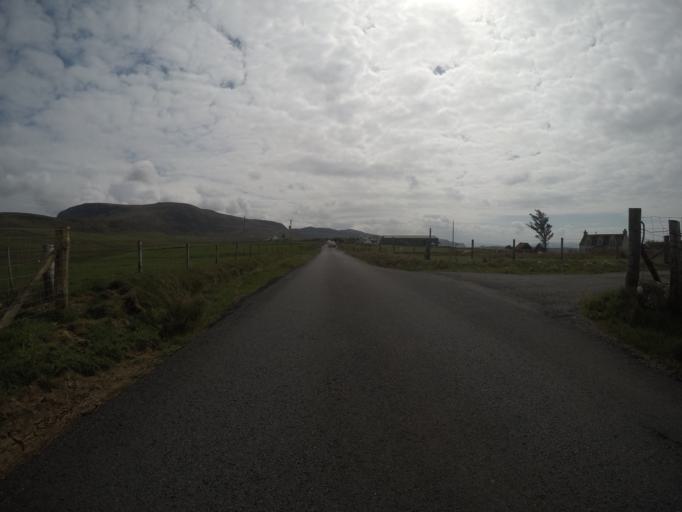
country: GB
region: Scotland
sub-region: Highland
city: Portree
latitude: 57.6453
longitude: -6.3787
